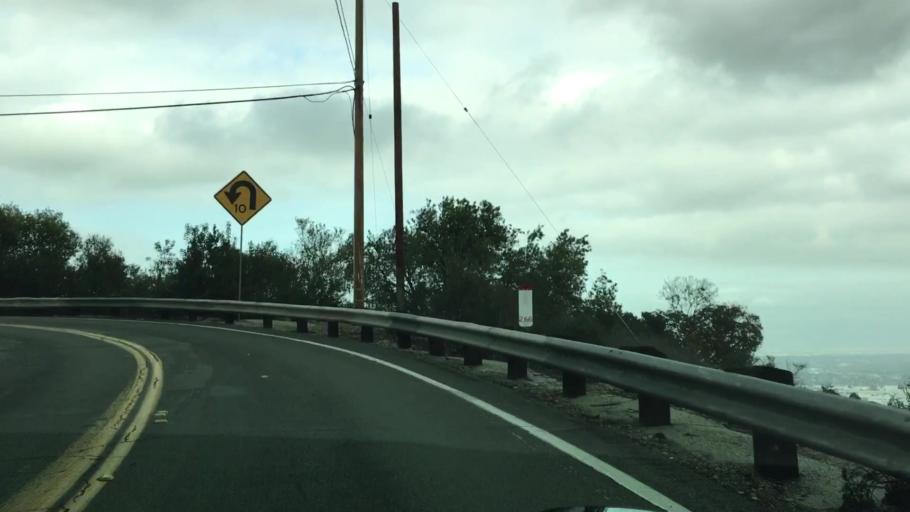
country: US
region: California
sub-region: Los Angeles County
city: Hacienda Heights
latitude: 33.9935
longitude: -117.9942
